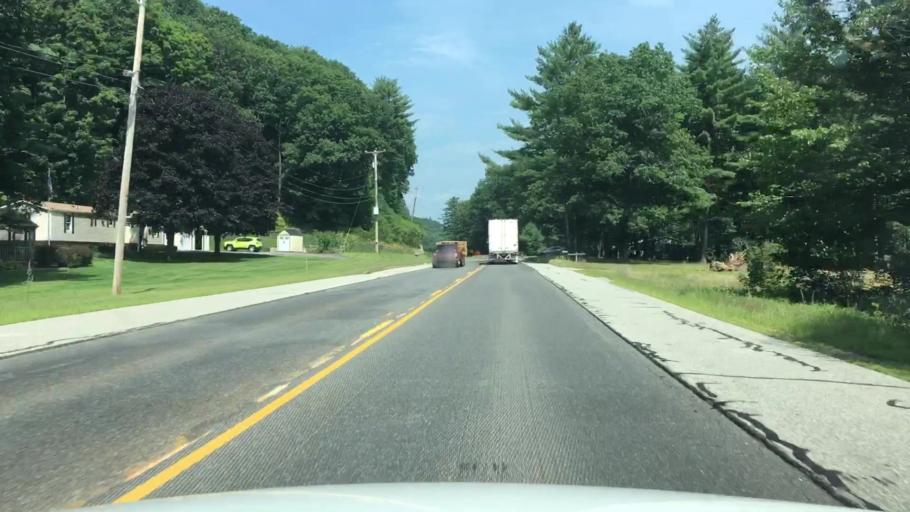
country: US
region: Maine
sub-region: Androscoggin County
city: Turner
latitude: 44.3067
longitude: -70.2664
